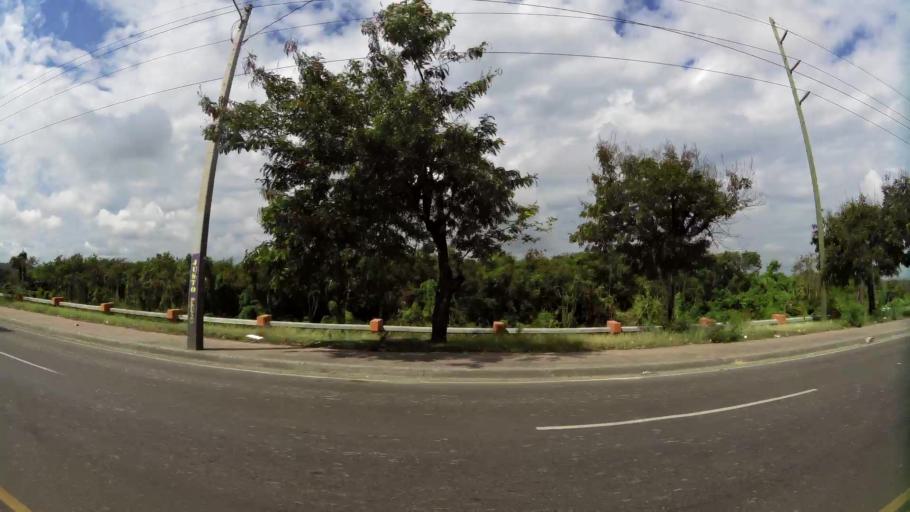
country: DO
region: Santiago
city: Santiago de los Caballeros
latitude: 19.4650
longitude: -70.7130
